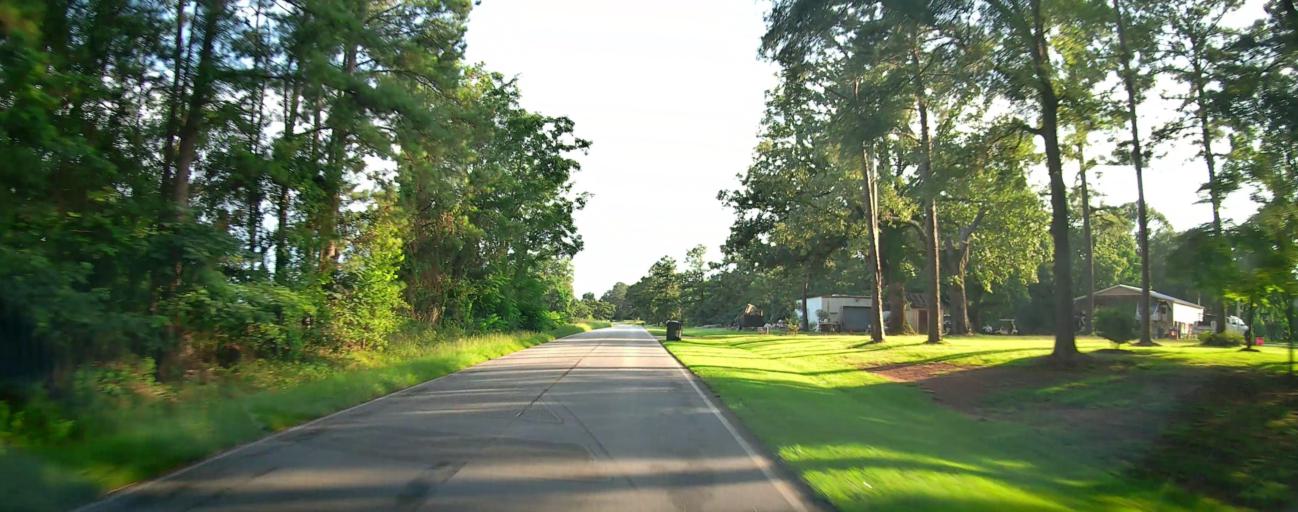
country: US
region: Georgia
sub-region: Peach County
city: Byron
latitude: 32.6884
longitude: -83.8552
